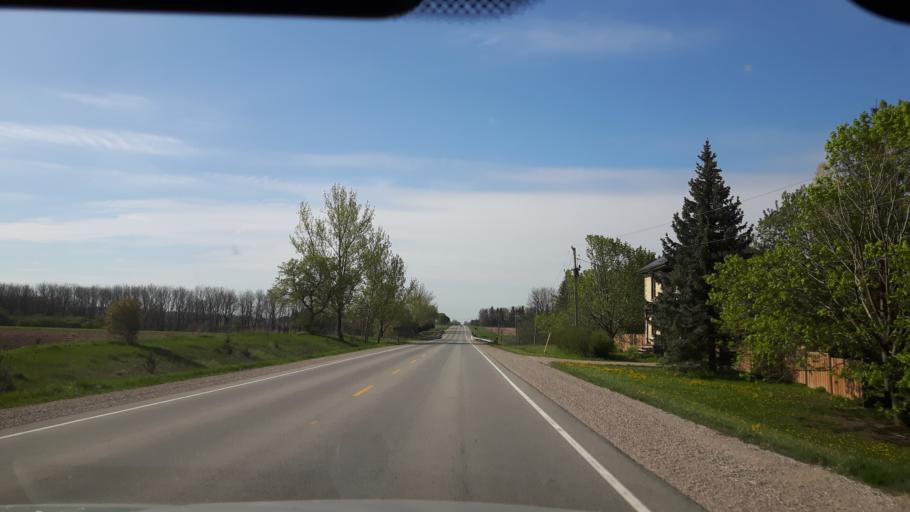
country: CA
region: Ontario
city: Bluewater
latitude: 43.4682
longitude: -81.5055
